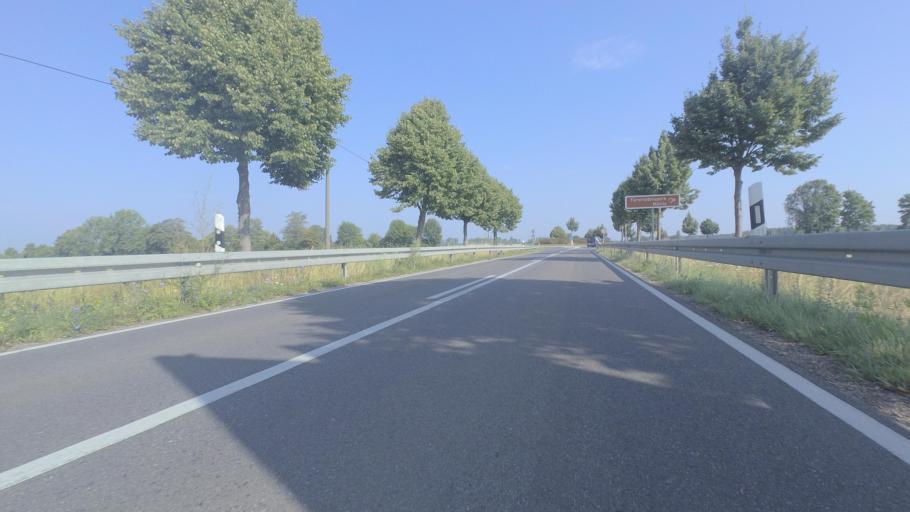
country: DE
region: Mecklenburg-Vorpommern
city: Malchow
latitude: 53.5178
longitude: 12.4231
